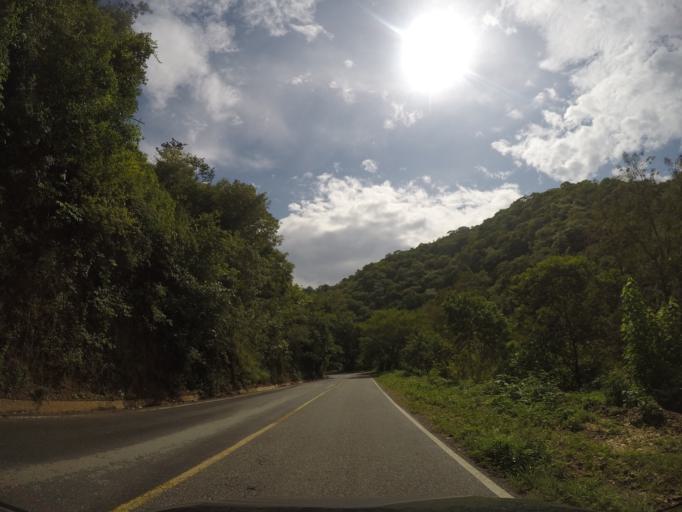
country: MX
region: Oaxaca
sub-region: San Jeronimo Coatlan
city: San Cristobal Honduras
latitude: 16.3621
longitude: -97.0895
